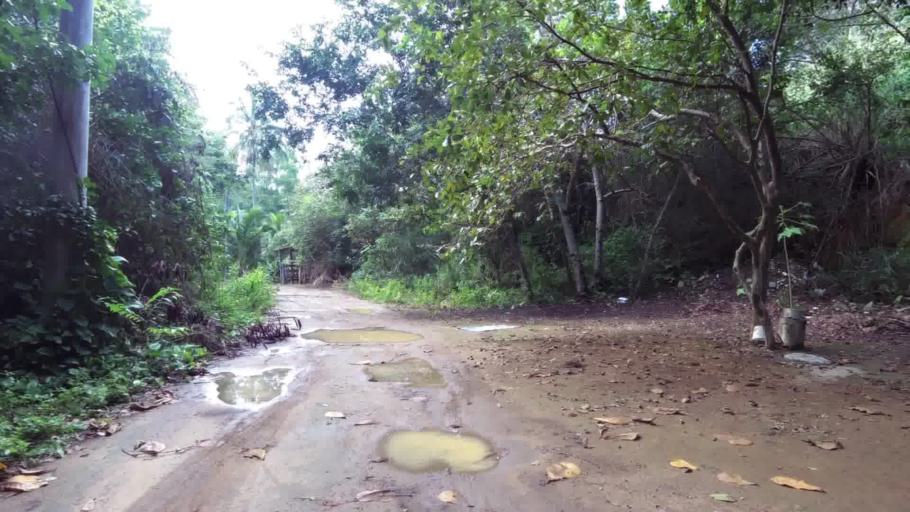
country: BR
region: Espirito Santo
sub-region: Piuma
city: Piuma
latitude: -20.8259
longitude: -40.6905
